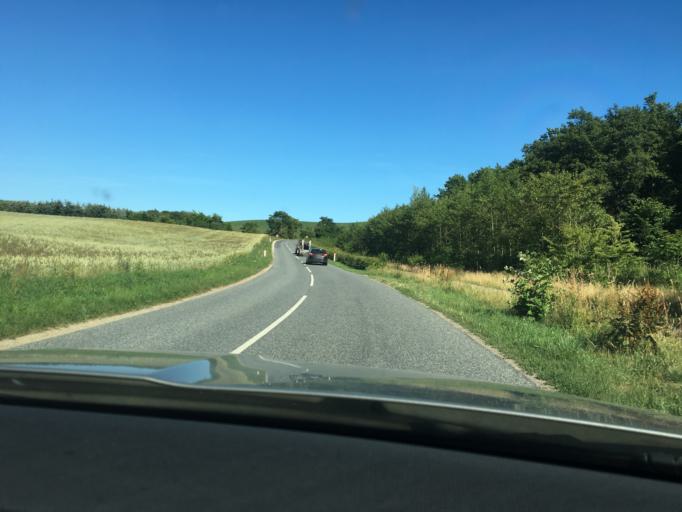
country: DK
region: Central Jutland
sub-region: Syddjurs Kommune
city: Hornslet
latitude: 56.3097
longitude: 10.3403
